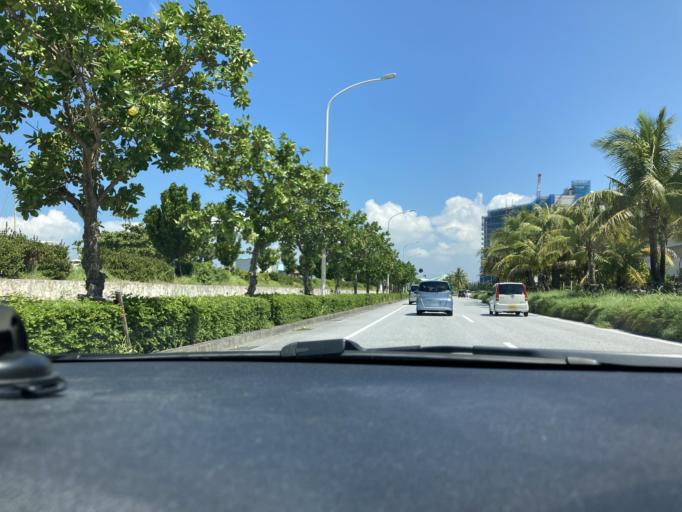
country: JP
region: Okinawa
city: Ginowan
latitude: 26.2753
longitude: 127.7290
